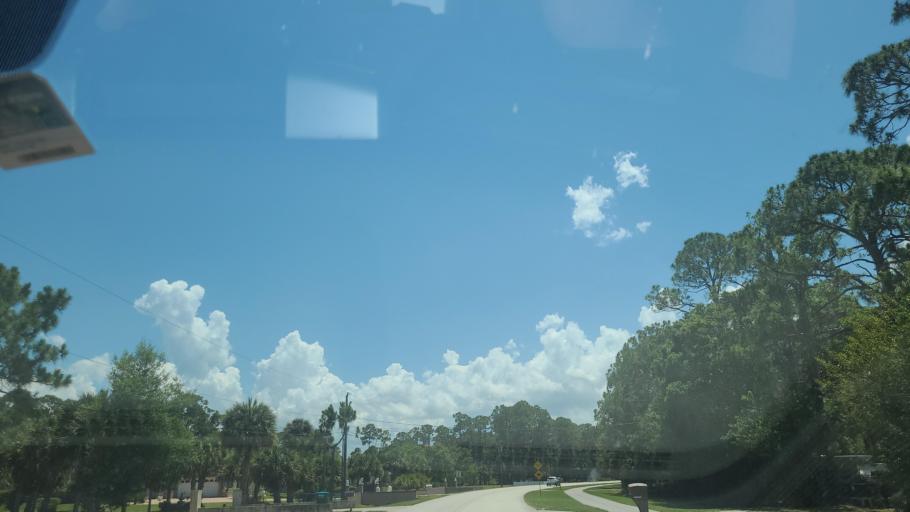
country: US
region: Florida
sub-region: Brevard County
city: Grant-Valkaria
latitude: 27.9556
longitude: -80.5705
